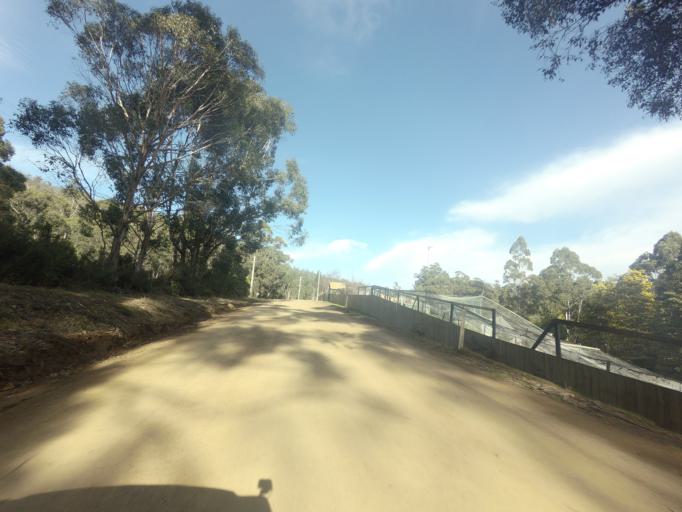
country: AU
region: Tasmania
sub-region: Huon Valley
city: Huonville
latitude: -43.0677
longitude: 147.0885
